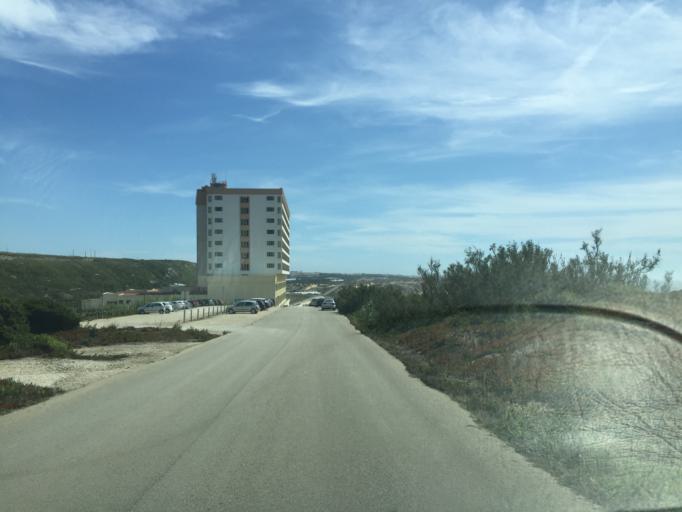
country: PT
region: Lisbon
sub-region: Lourinha
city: Lourinha
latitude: 39.1815
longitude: -9.3548
